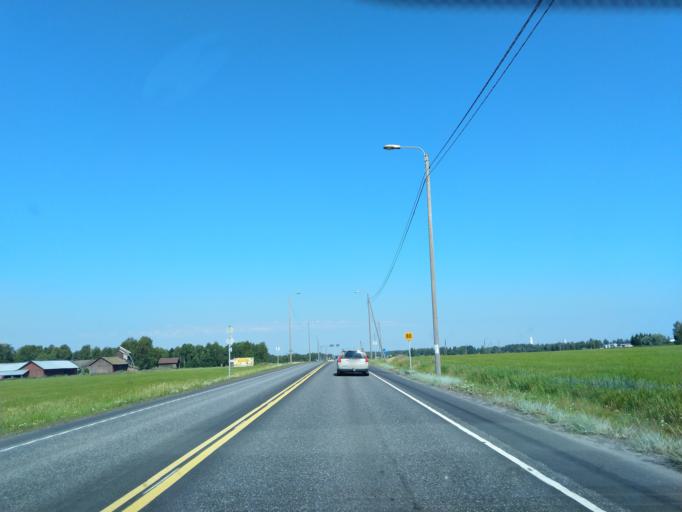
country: FI
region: Satakunta
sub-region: Pori
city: Nakkila
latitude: 61.3482
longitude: 22.0174
